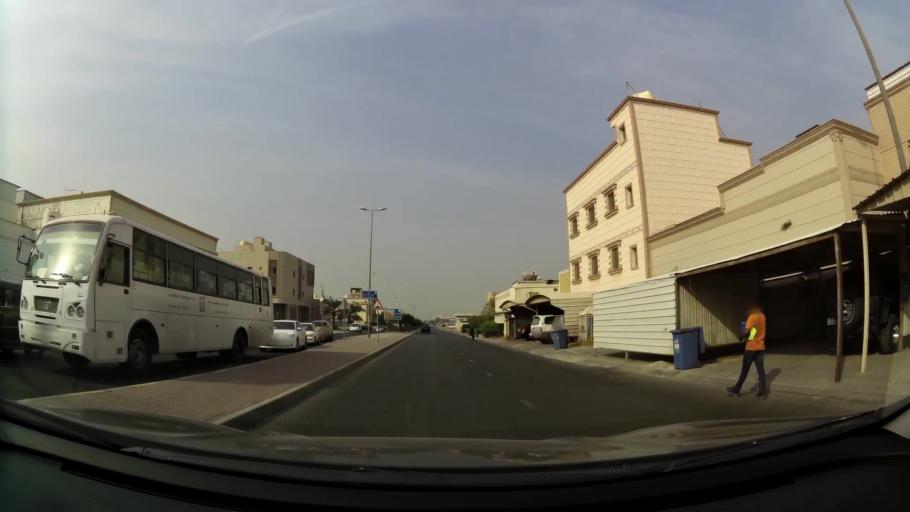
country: KW
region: Al Farwaniyah
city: Al Farwaniyah
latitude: 29.2908
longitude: 47.9546
